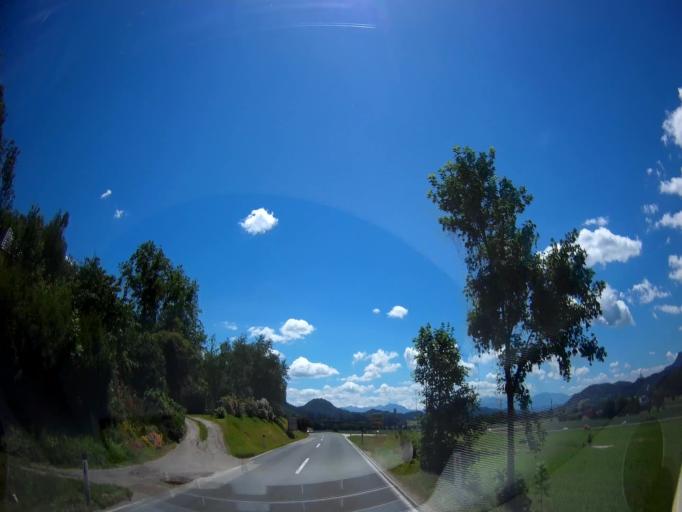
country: AT
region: Carinthia
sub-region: Politischer Bezirk Sankt Veit an der Glan
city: Sankt Veit an der Glan
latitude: 46.7433
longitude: 14.3899
